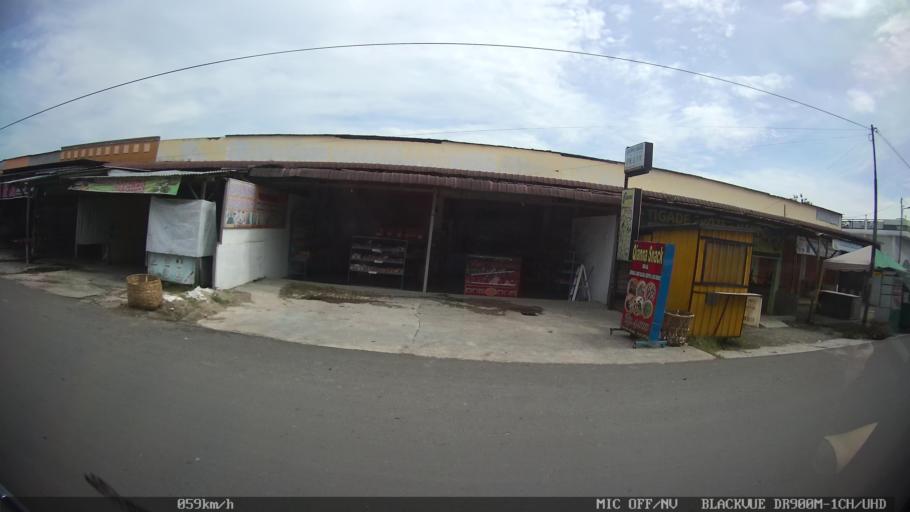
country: ID
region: North Sumatra
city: Percut
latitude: 3.6127
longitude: 98.8069
